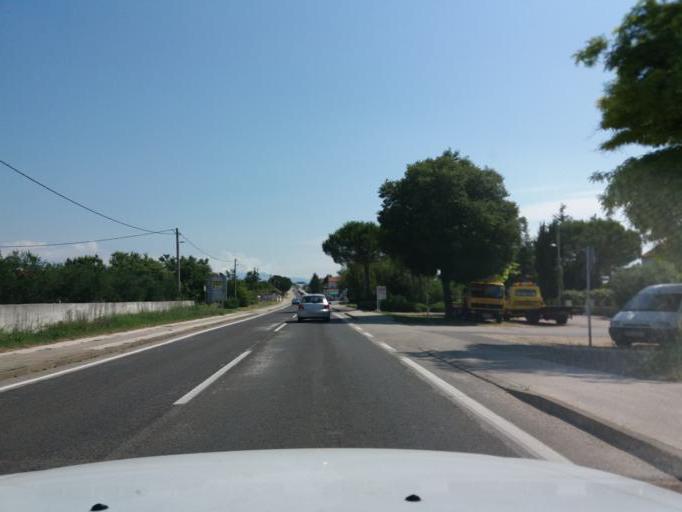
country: HR
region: Zadarska
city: Policnik
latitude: 44.1427
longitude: 15.3169
